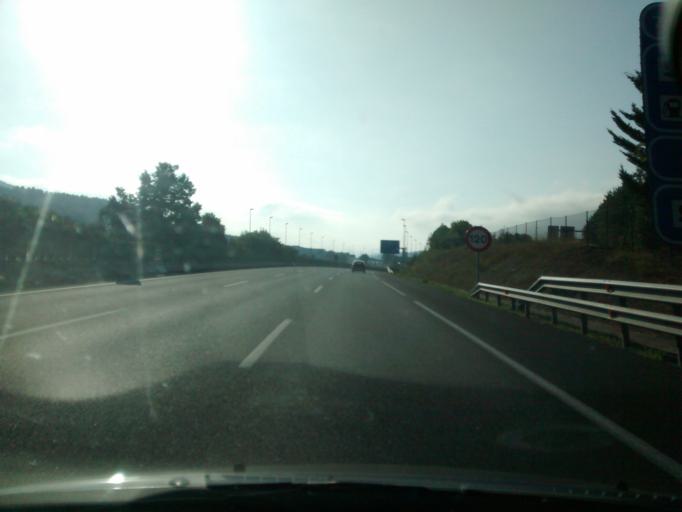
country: ES
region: Basque Country
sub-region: Bizkaia
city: Amorebieta
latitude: 43.2265
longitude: -2.7405
